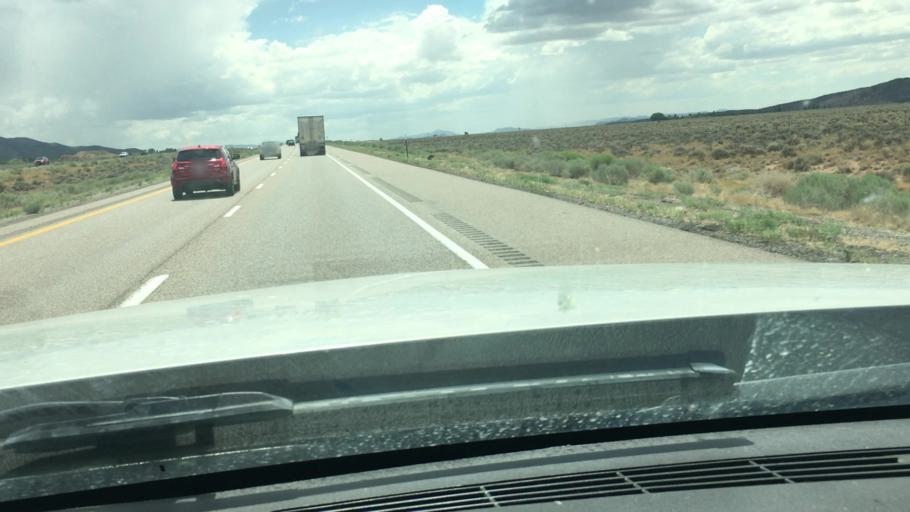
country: US
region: Utah
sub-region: Iron County
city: Parowan
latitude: 37.8199
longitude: -112.9178
